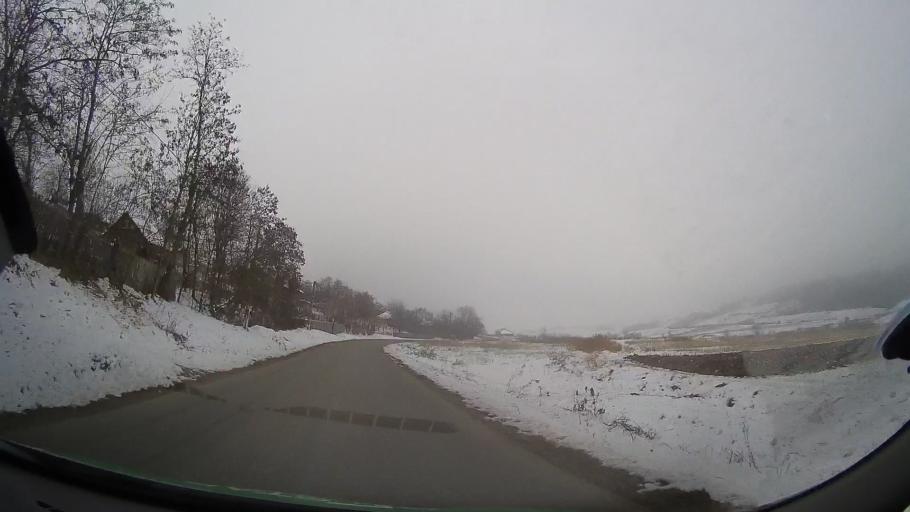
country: RO
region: Bacau
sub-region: Comuna Vultureni
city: Vultureni
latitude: 46.3524
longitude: 27.2886
